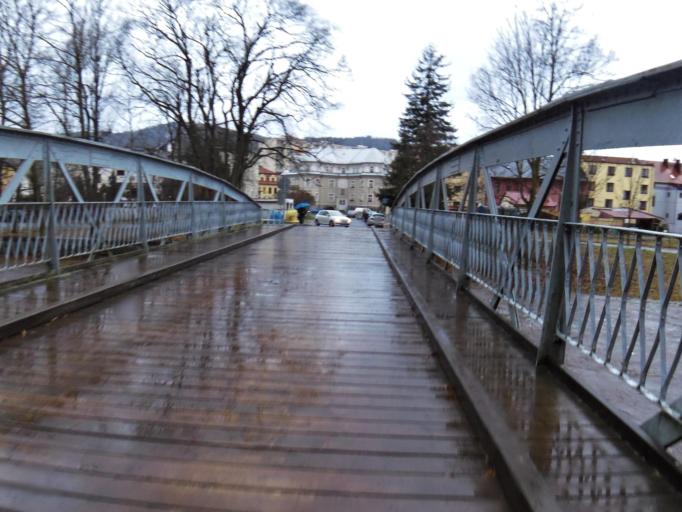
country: CZ
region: Plzensky
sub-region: Okres Klatovy
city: Susice
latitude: 49.2366
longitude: 13.5247
